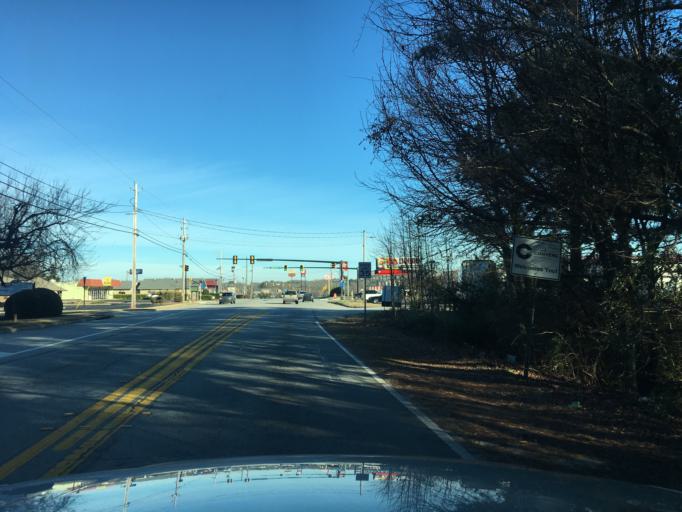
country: US
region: Georgia
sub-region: Rockdale County
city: Conyers
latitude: 33.6647
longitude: -84.0365
